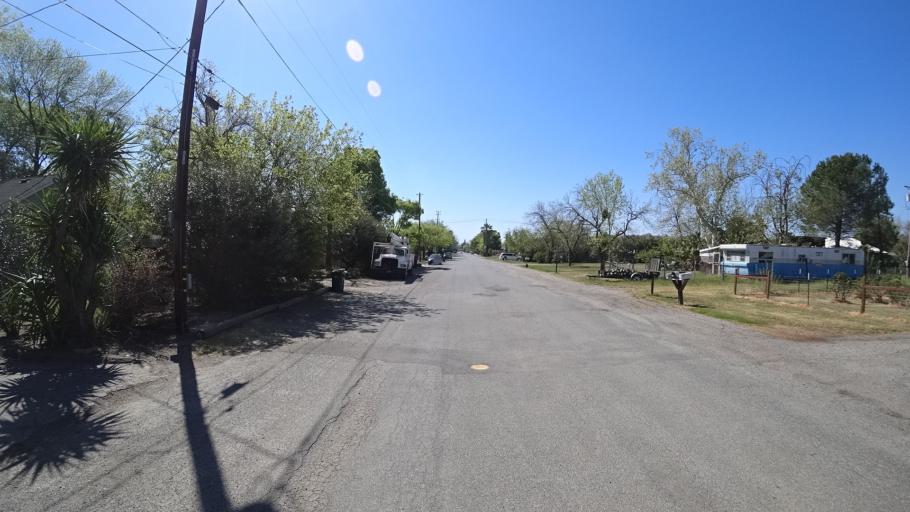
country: US
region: California
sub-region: Glenn County
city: Willows
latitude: 39.5301
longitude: -122.1881
